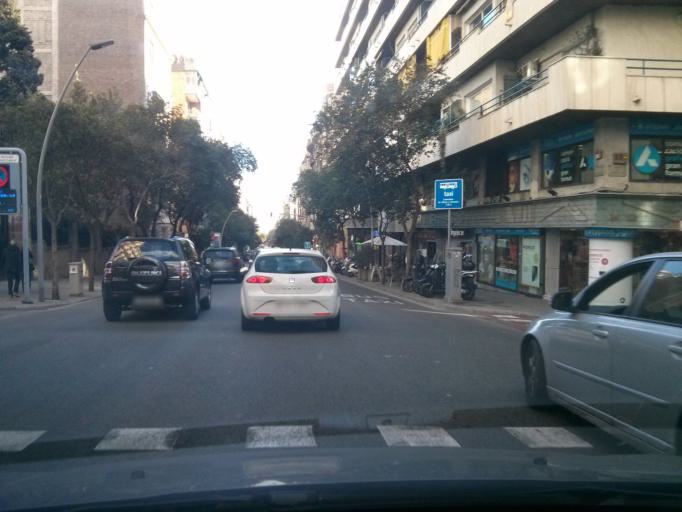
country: ES
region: Catalonia
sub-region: Provincia de Barcelona
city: Sarria-Sant Gervasi
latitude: 41.3965
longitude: 2.1465
